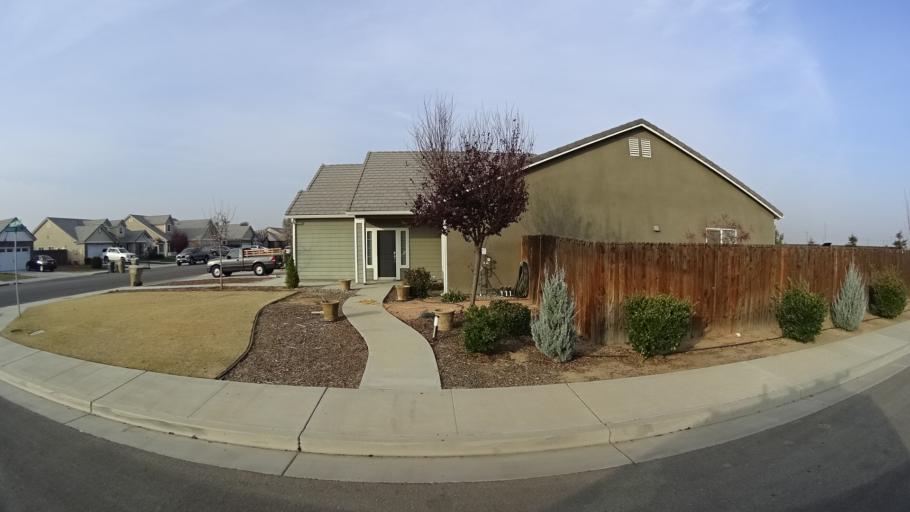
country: US
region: California
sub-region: Kern County
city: Greenacres
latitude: 35.4376
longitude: -119.1167
